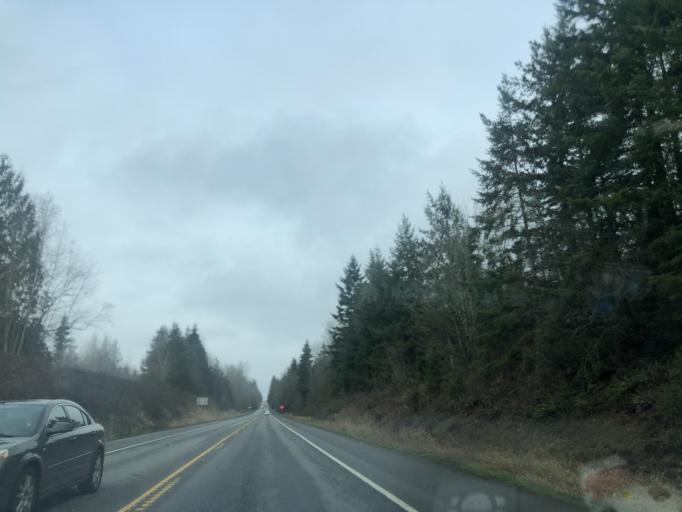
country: US
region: Washington
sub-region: Snohomish County
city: Sisco Heights
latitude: 48.0753
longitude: -122.1114
